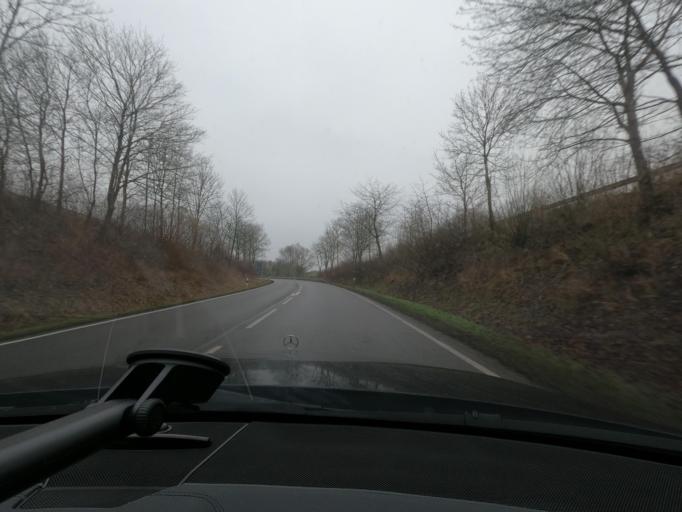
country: DE
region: Hesse
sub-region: Regierungsbezirk Kassel
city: Volkmarsen
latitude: 51.3399
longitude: 9.0965
